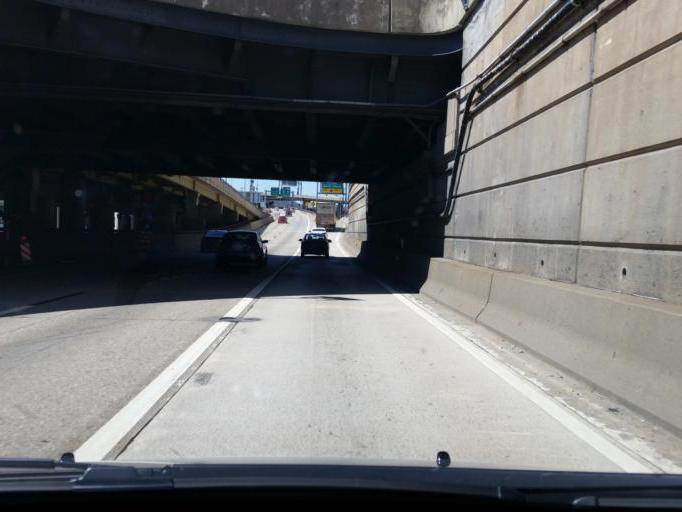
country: US
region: Pennsylvania
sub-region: Allegheny County
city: Pittsburgh
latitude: 40.4383
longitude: -80.0054
